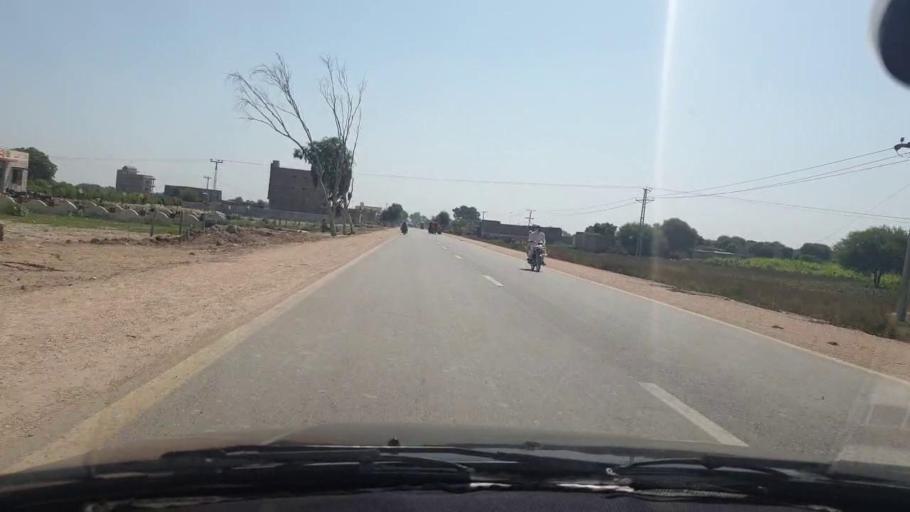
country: PK
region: Sindh
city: Tando Allahyar
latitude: 25.4467
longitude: 68.7304
